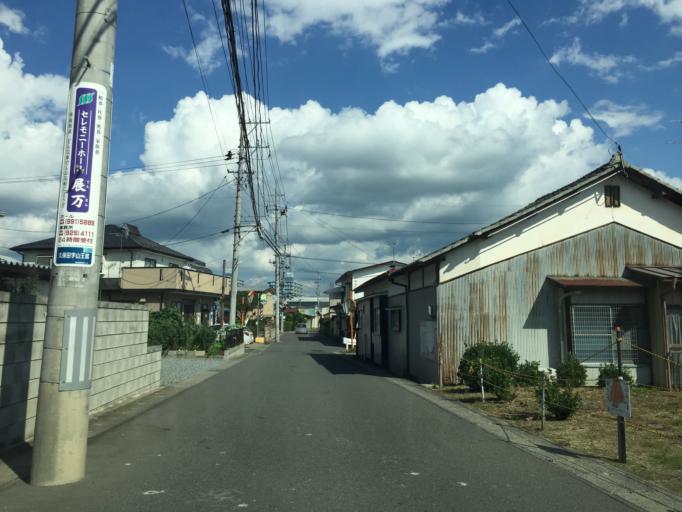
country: JP
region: Fukushima
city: Koriyama
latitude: 37.4094
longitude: 140.3873
